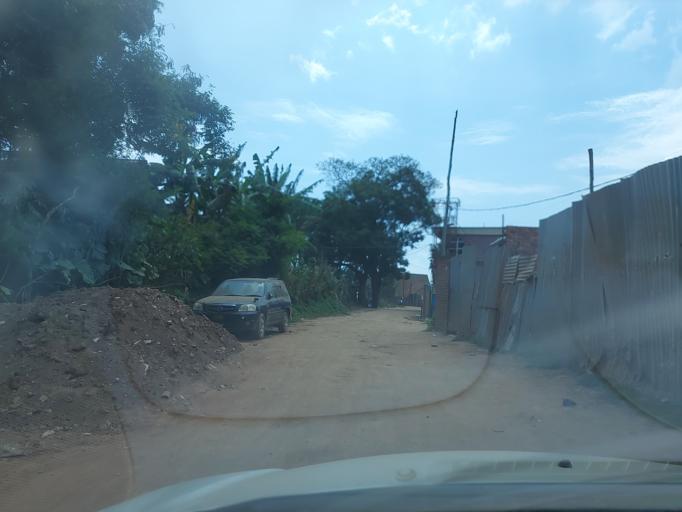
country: CD
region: South Kivu
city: Bukavu
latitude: -2.4960
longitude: 28.8623
